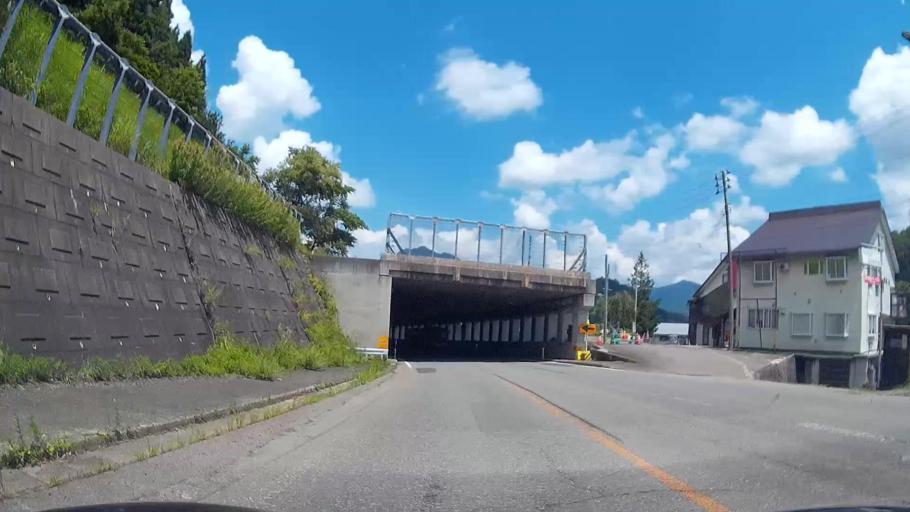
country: JP
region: Niigata
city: Shiozawa
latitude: 36.9182
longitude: 138.8070
